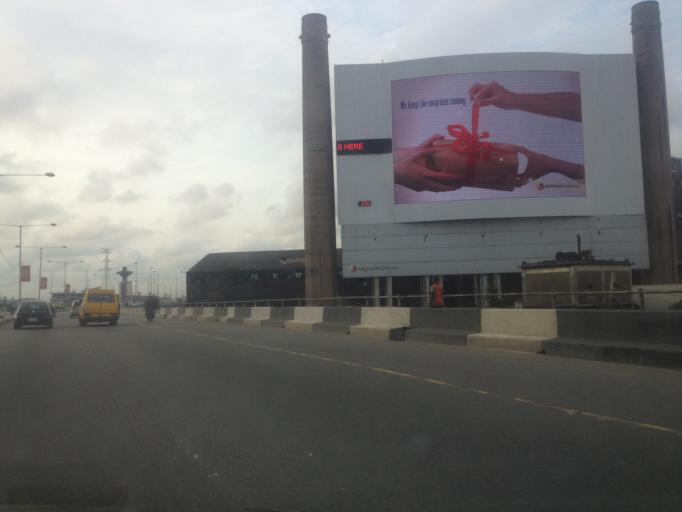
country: NG
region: Lagos
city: Lagos
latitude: 6.4659
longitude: 3.3793
